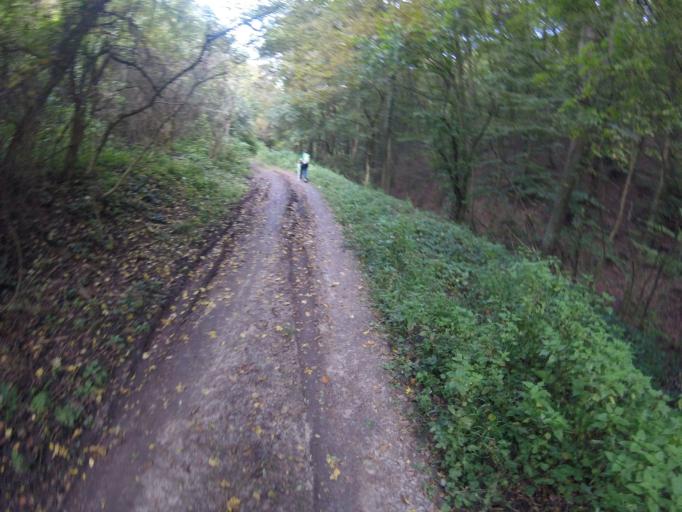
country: HU
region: Pest
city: Szob
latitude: 47.8047
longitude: 18.8362
